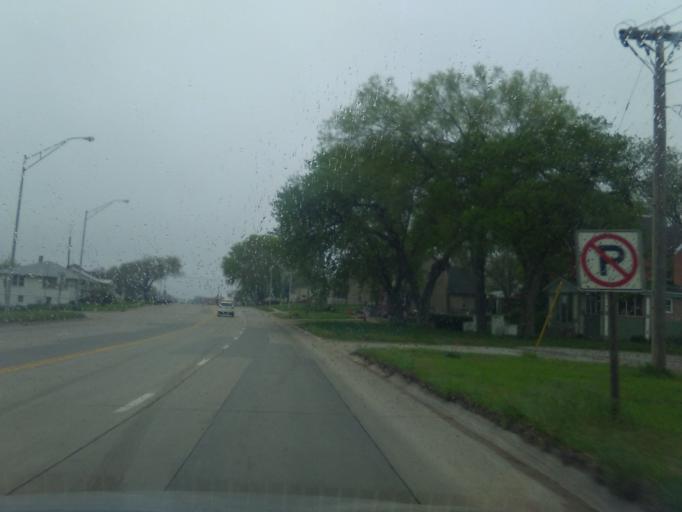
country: US
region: Nebraska
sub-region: Cuming County
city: Wisner
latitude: 41.9844
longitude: -96.9091
